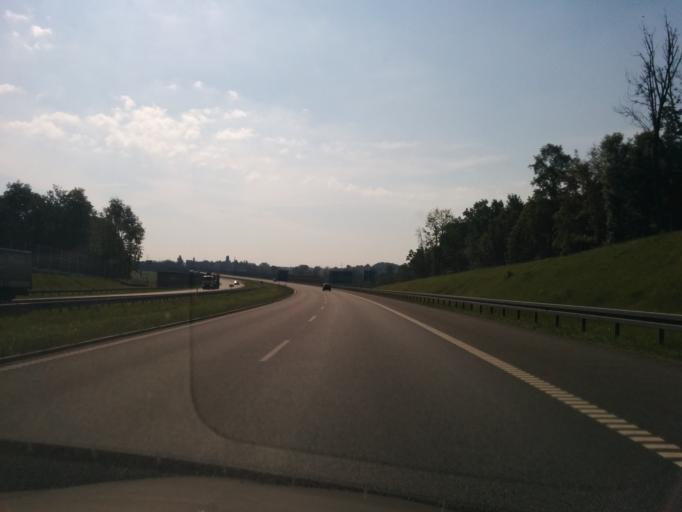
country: PL
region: Silesian Voivodeship
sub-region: Powiat tarnogorski
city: Radzionkow
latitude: 50.3742
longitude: 18.8800
